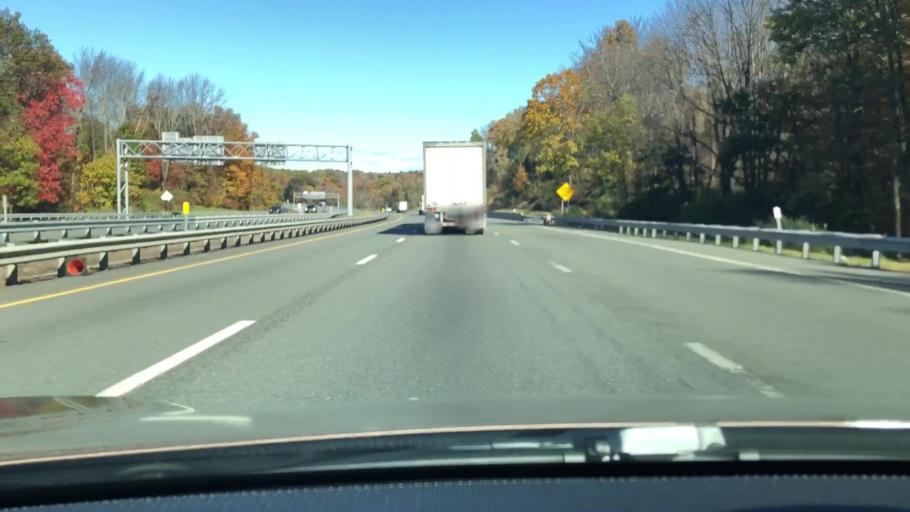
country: US
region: New York
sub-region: Orange County
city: Central Valley
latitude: 41.3167
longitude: -74.1154
